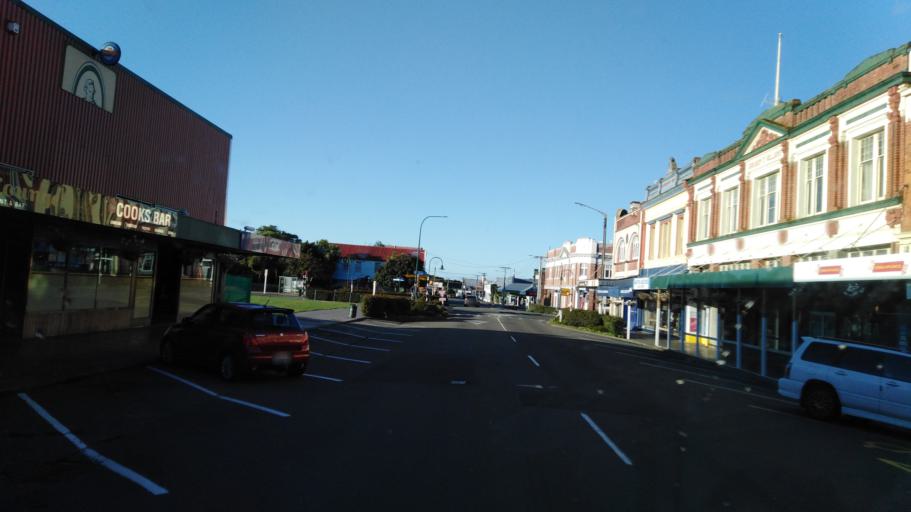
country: NZ
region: Manawatu-Wanganui
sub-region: Rangitikei District
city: Bulls
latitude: -40.0684
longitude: 175.3786
